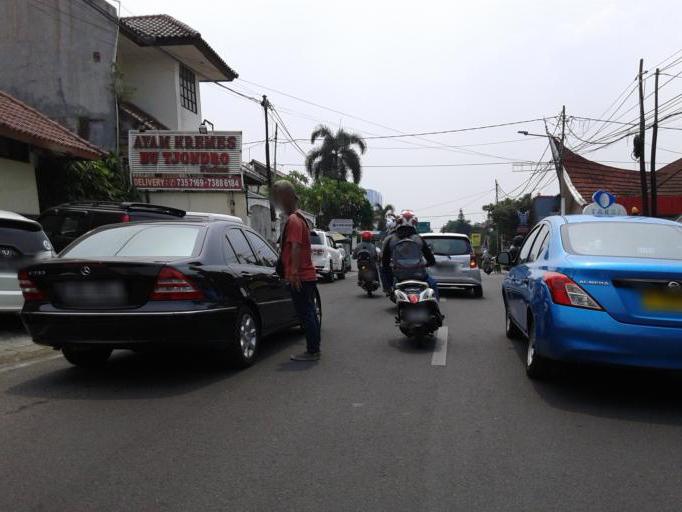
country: ID
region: Banten
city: South Tangerang
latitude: -6.2723
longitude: 106.7536
